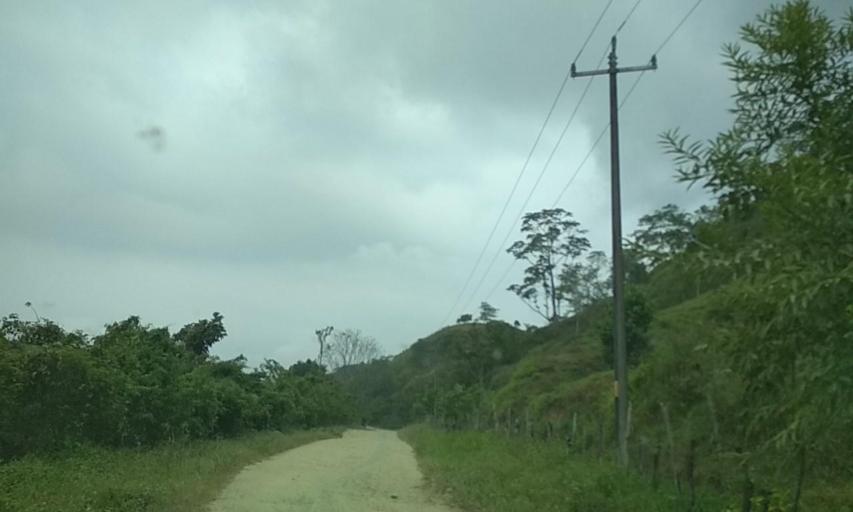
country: MX
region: Veracruz
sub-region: Uxpanapa
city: Poblado 10
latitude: 17.4521
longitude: -94.0869
